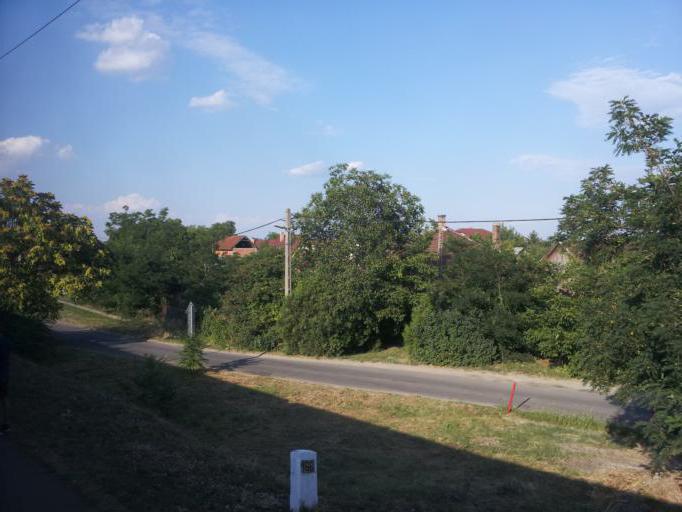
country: HU
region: Pest
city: Dunaharaszti
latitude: 47.3405
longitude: 19.0874
